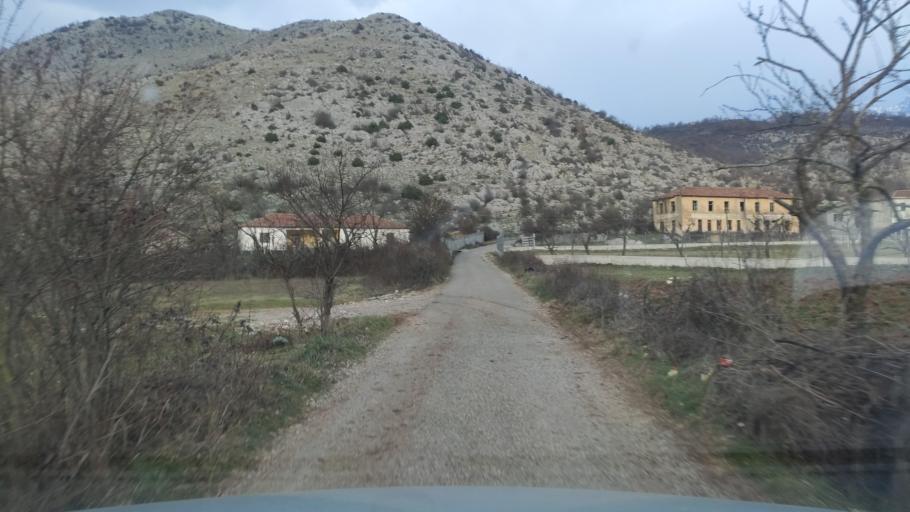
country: AL
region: Shkoder
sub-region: Rrethi i Malesia e Madhe
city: Gruemire
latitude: 42.2381
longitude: 19.5304
